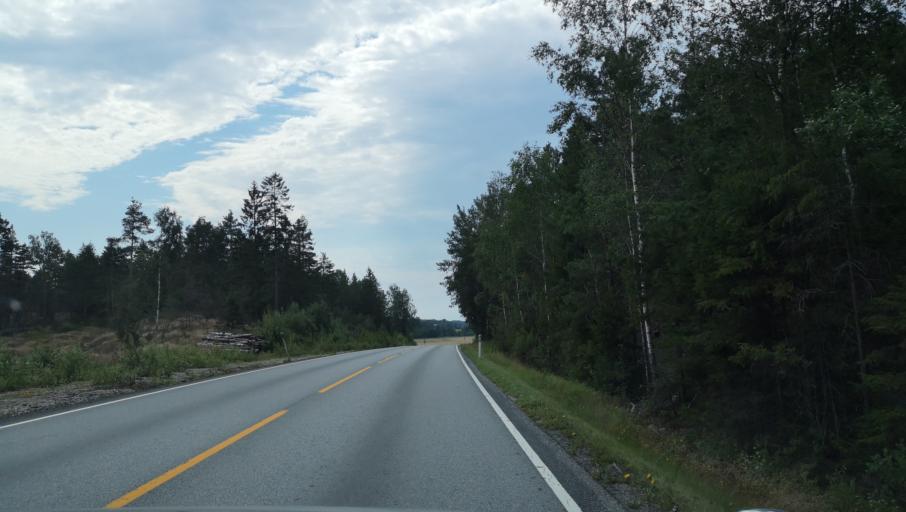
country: NO
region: Ostfold
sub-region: Valer
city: Kirkebygda
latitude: 59.4805
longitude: 10.7937
